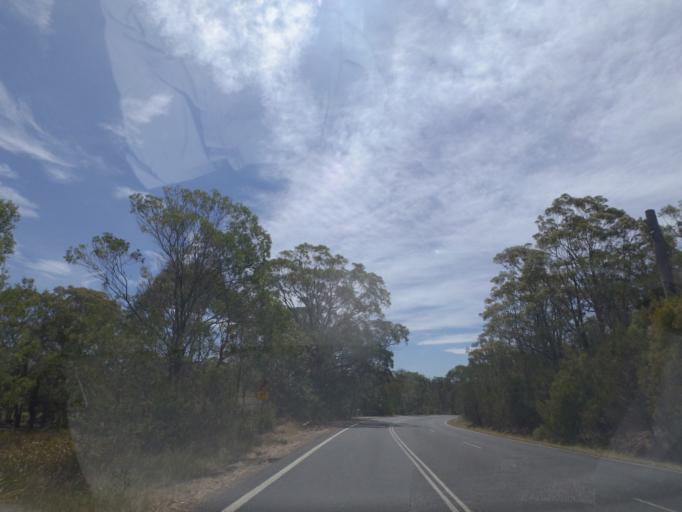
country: AU
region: New South Wales
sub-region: Wingecarribee
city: Colo Vale
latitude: -34.3933
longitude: 150.5315
